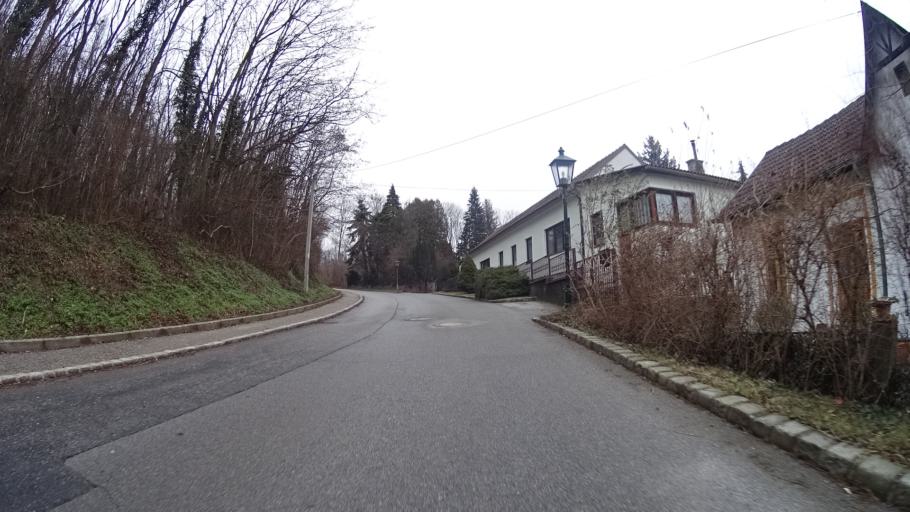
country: AT
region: Lower Austria
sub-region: Politischer Bezirk Korneuburg
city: Leobendorf
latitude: 48.3732
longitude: 16.3108
